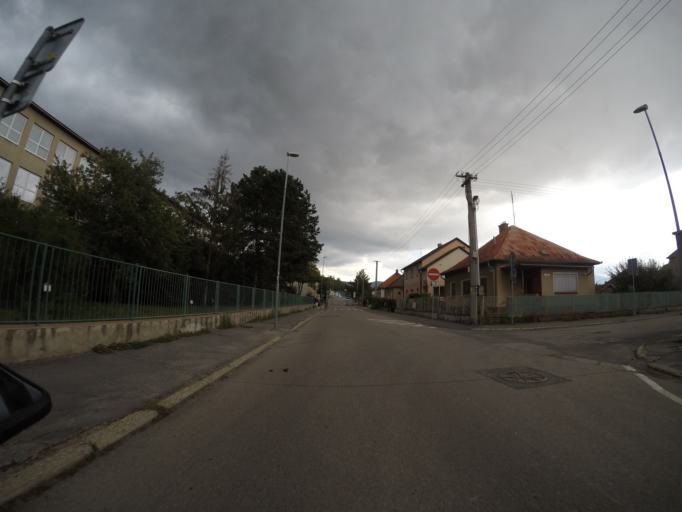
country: SK
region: Trenciansky
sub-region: Okres Trencin
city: Trencin
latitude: 48.8761
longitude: 18.0332
